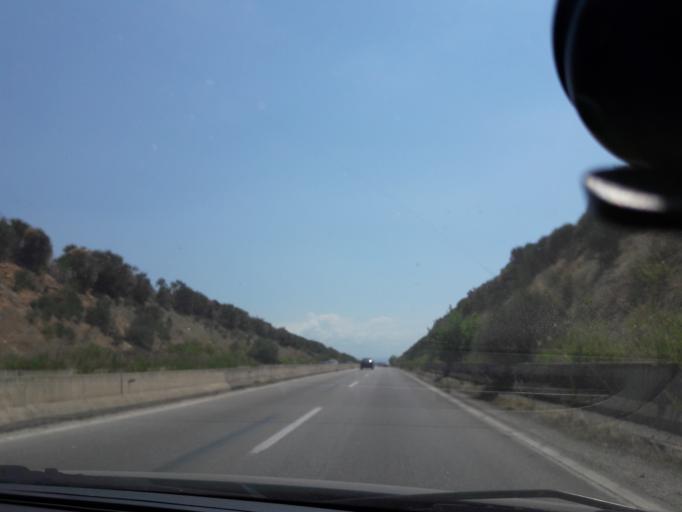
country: GR
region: Central Macedonia
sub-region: Nomos Chalkidikis
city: Nea Triglia
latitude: 40.2975
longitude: 23.1379
